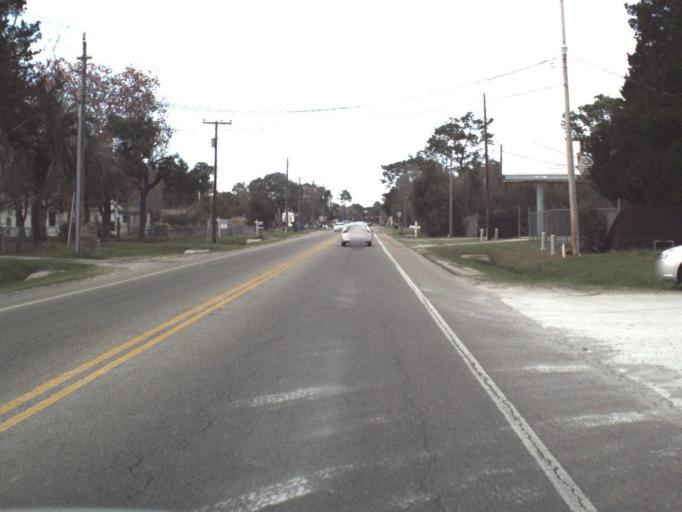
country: US
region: Florida
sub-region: Bay County
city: Hiland Park
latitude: 30.1938
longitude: -85.6249
